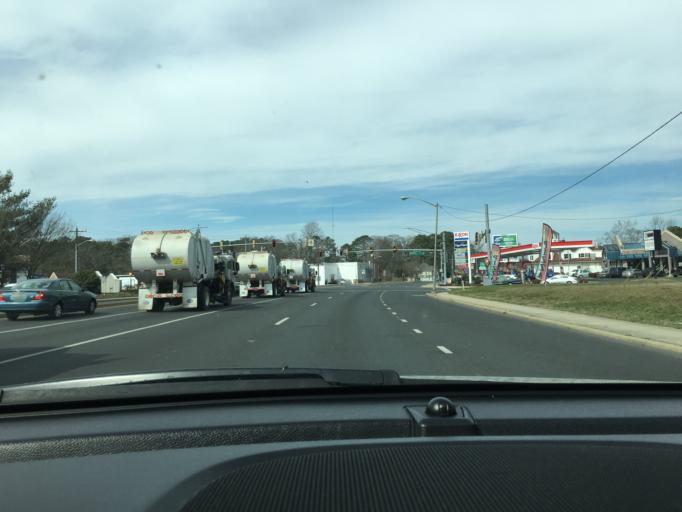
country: US
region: Maryland
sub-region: Wicomico County
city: Salisbury
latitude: 38.3692
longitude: -75.6134
